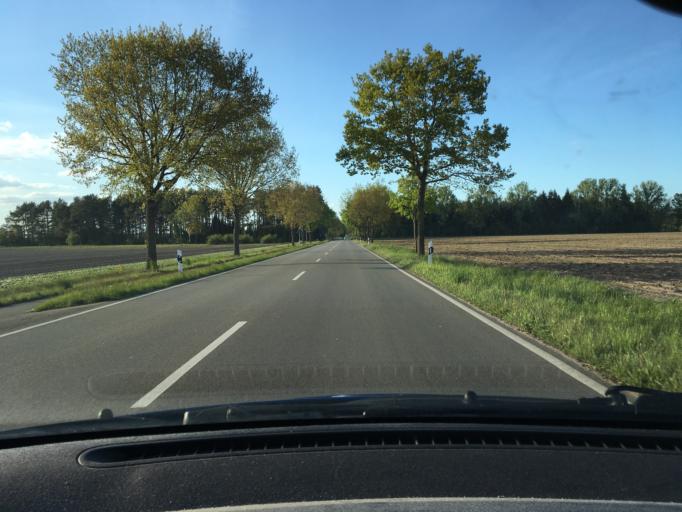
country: DE
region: Lower Saxony
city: Oldendorf
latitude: 53.1622
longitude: 10.2127
